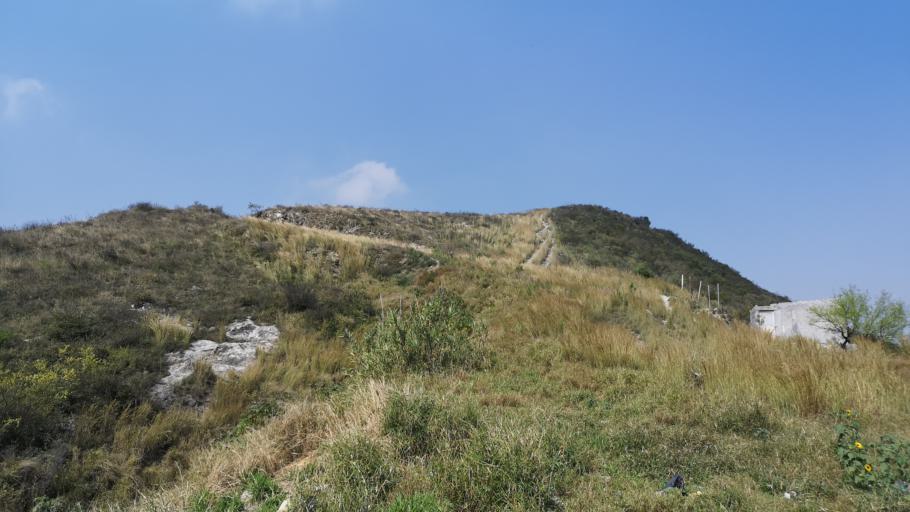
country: MX
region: Nuevo Leon
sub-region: Monterrey
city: Monterrey
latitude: 25.6501
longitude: -100.3190
